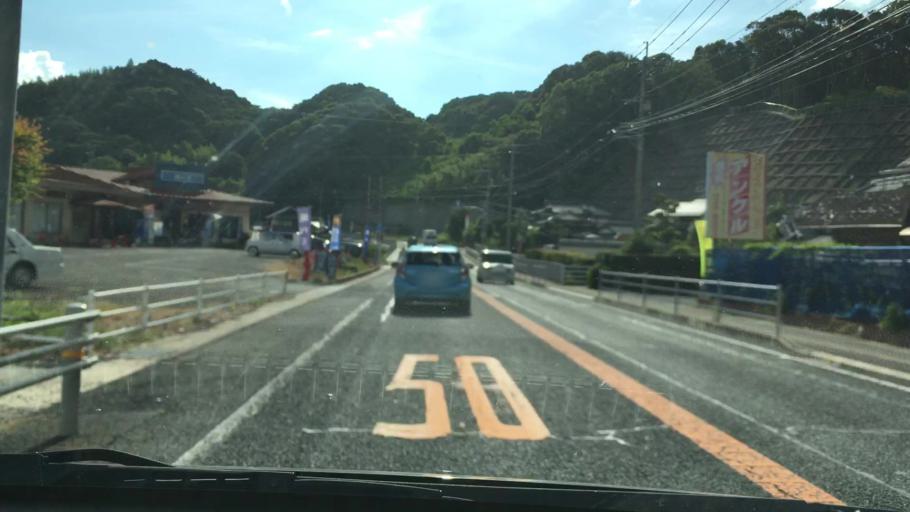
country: JP
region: Nagasaki
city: Sasebo
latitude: 33.1650
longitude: 129.8366
